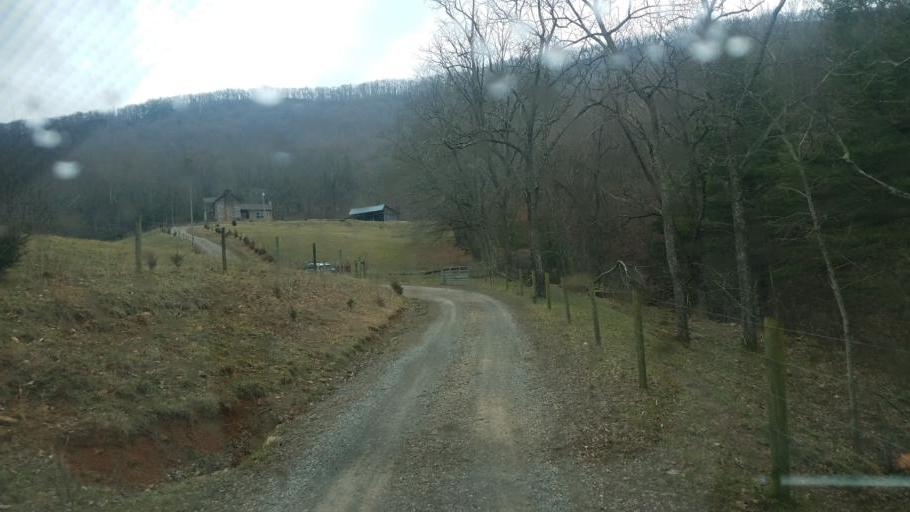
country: US
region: Virginia
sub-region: Pulaski County
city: Dublin
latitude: 37.2181
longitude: -80.7009
